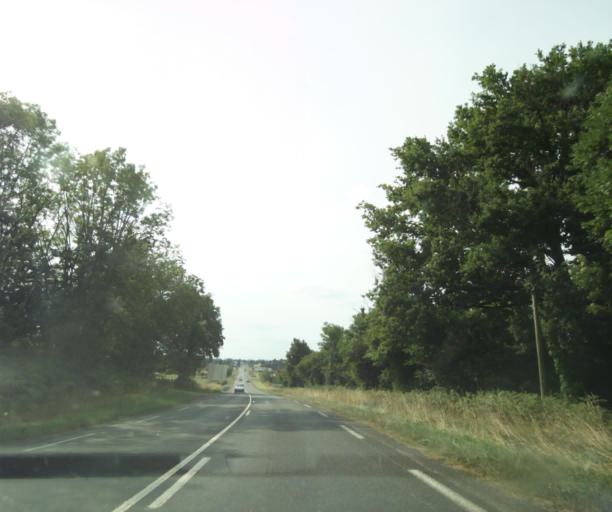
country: FR
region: Pays de la Loire
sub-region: Departement de la Sarthe
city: Ecommoy
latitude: 47.8208
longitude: 0.2968
